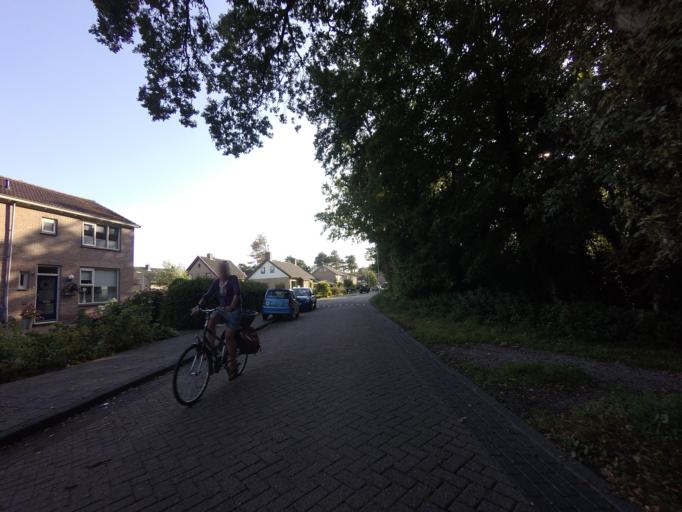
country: NL
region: Friesland
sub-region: Gemeente Terschelling
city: West-Terschelling
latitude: 53.3682
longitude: 5.2138
